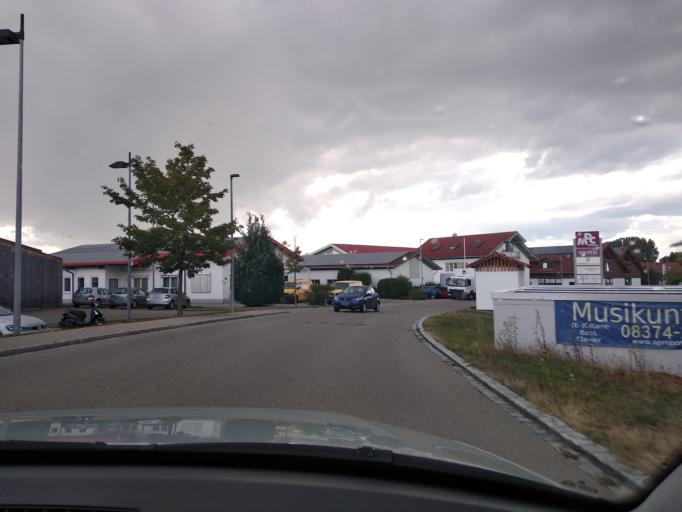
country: DE
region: Bavaria
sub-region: Swabia
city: Dietmannsried
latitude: 47.8060
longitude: 10.2979
